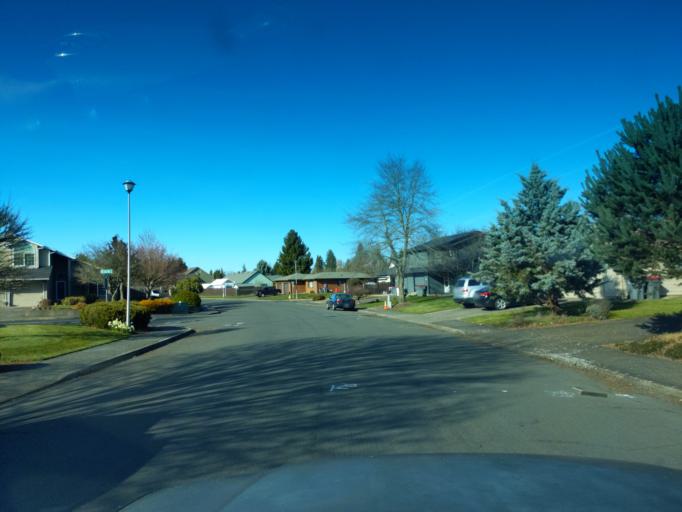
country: US
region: Oregon
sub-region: Yamhill County
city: McMinnville
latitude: 45.2000
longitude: -123.2138
